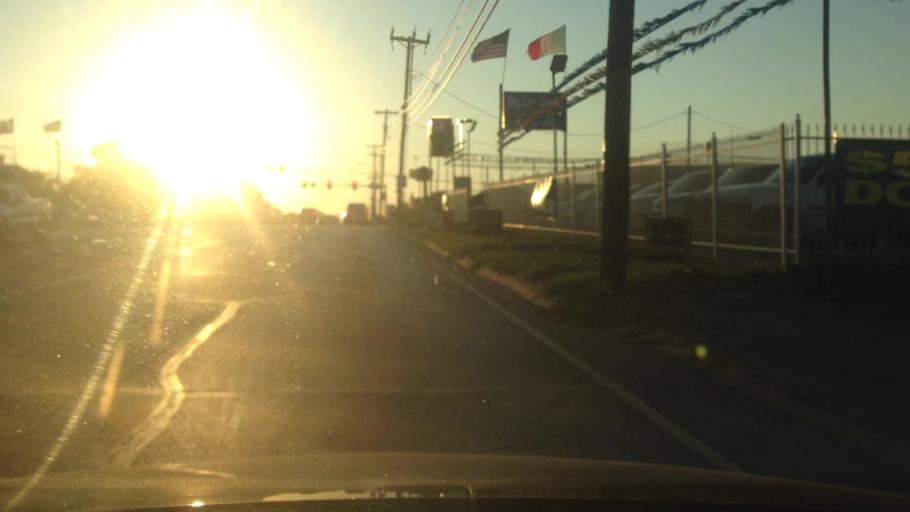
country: US
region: Texas
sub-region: Tarrant County
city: Haltom City
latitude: 32.7951
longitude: -97.2919
